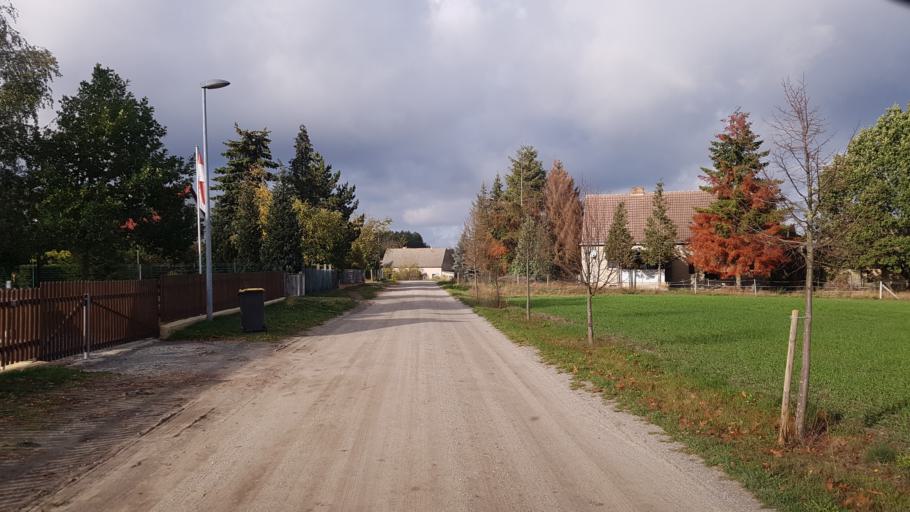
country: DE
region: Brandenburg
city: Schonborn
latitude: 51.6120
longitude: 13.5176
